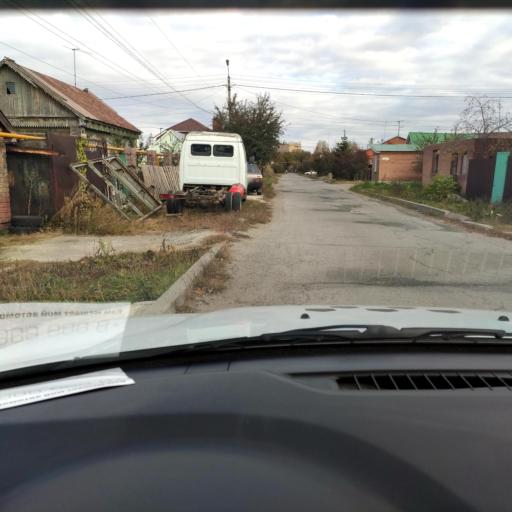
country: RU
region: Samara
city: Tol'yatti
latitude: 53.5271
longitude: 49.4269
